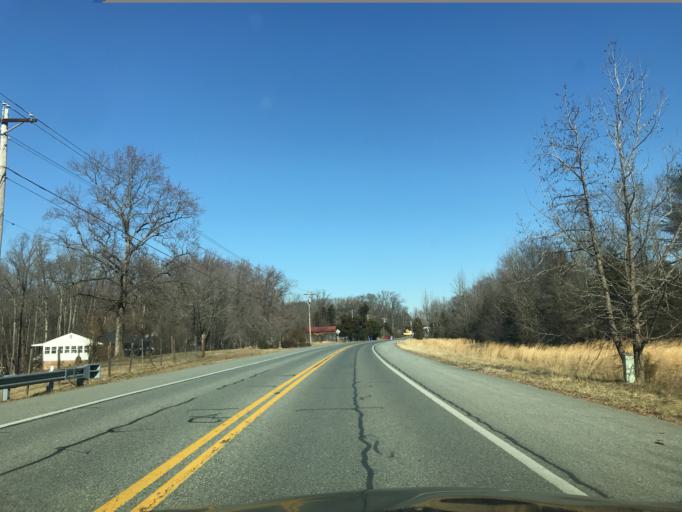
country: US
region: Maryland
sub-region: Charles County
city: Indian Head
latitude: 38.5696
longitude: -77.1597
